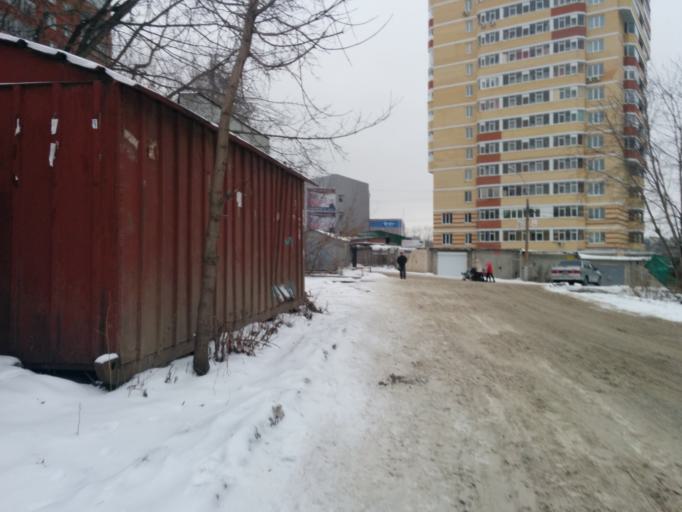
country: RU
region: Perm
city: Perm
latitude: 57.9974
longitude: 56.2068
